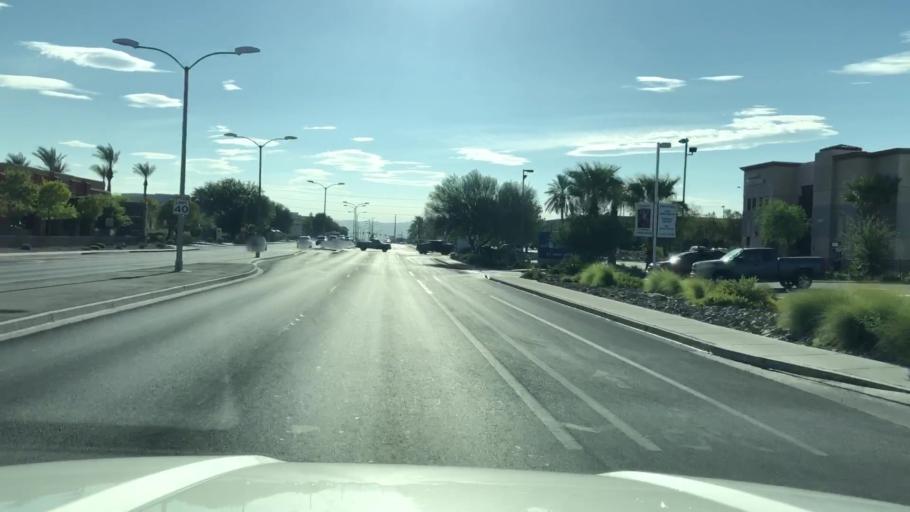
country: US
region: Nevada
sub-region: Clark County
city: Whitney
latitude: 36.0561
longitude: -115.0520
